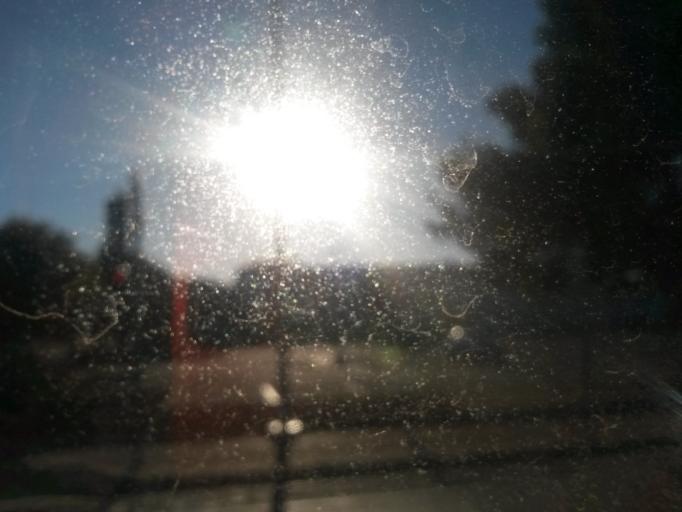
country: AU
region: South Australia
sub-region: Charles Sturt
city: Woodville North
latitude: -34.8725
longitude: 138.5483
